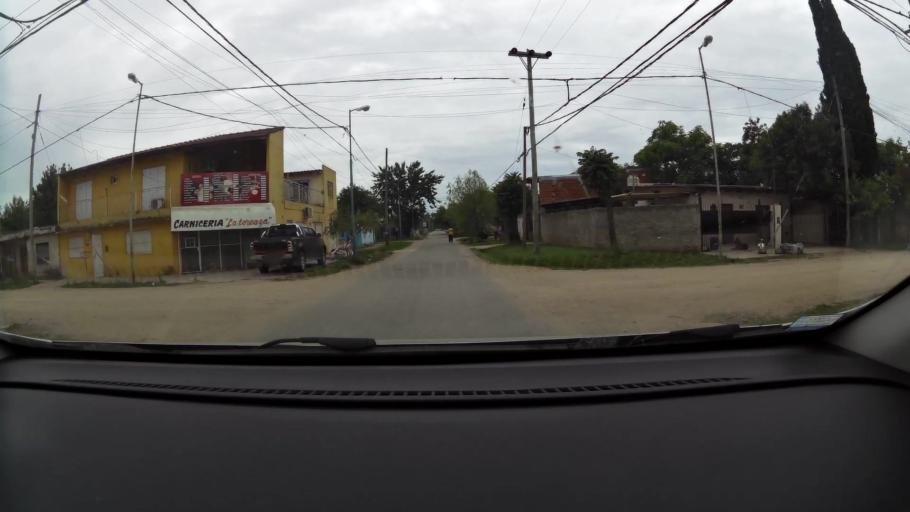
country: AR
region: Buenos Aires
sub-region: Partido de Zarate
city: Zarate
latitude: -34.1141
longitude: -59.0295
